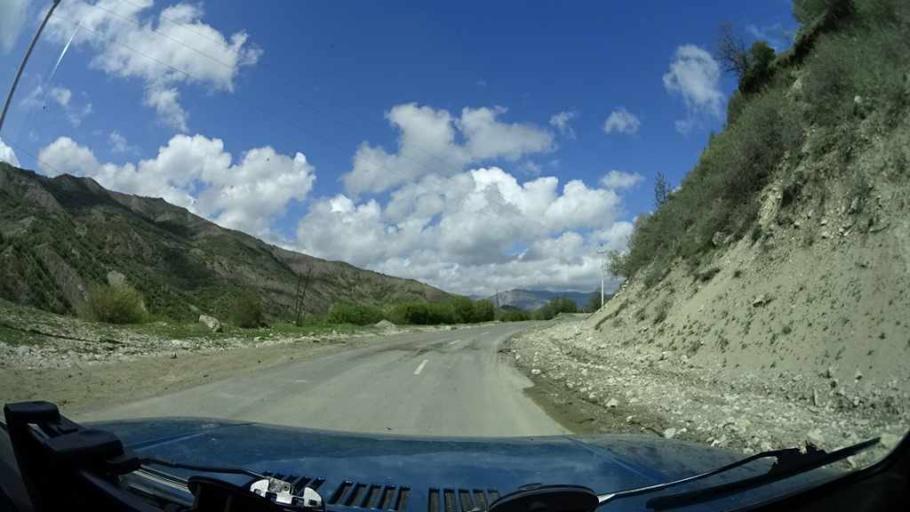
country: AZ
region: Ismayilli
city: Basqal
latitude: 40.8416
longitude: 48.3712
